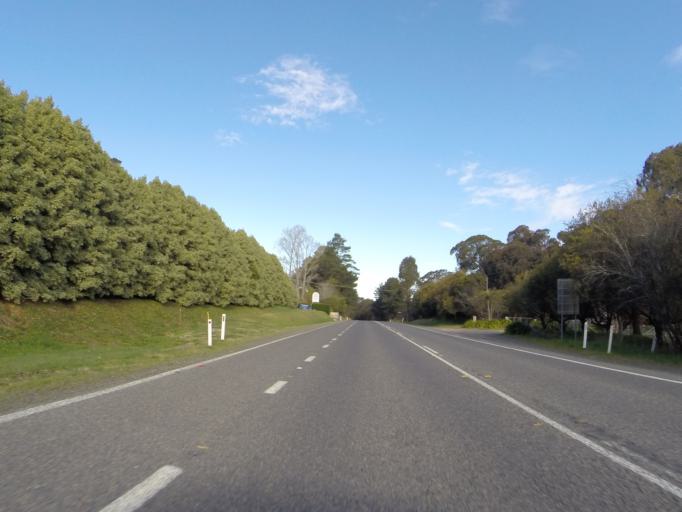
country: AU
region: New South Wales
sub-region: Wingecarribee
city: Moss Vale
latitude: -34.5627
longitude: 150.4023
